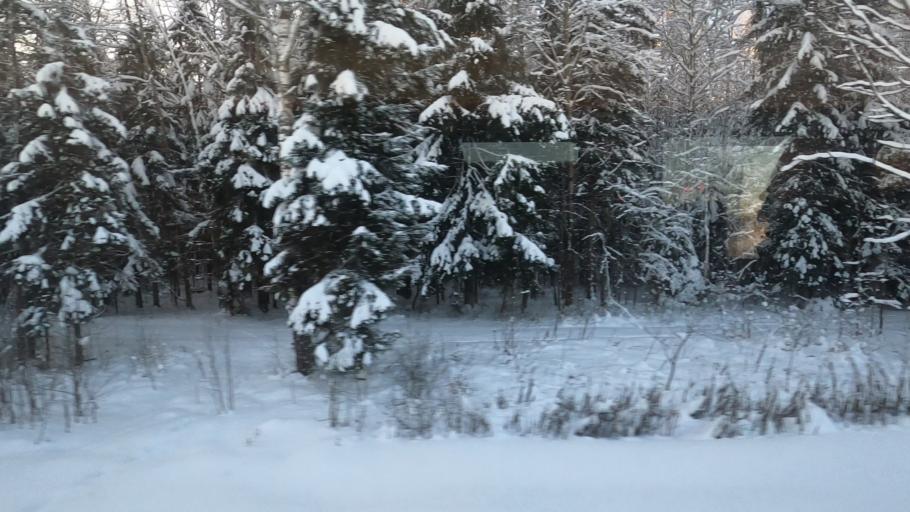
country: RU
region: Moskovskaya
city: Taldom
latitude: 56.6578
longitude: 37.5676
